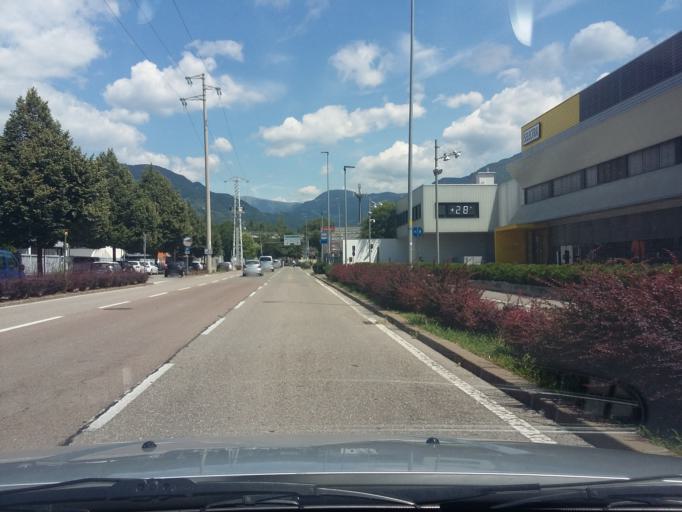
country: IT
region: Trentino-Alto Adige
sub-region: Bolzano
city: Bolzano
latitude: 46.4836
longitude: 11.3318
